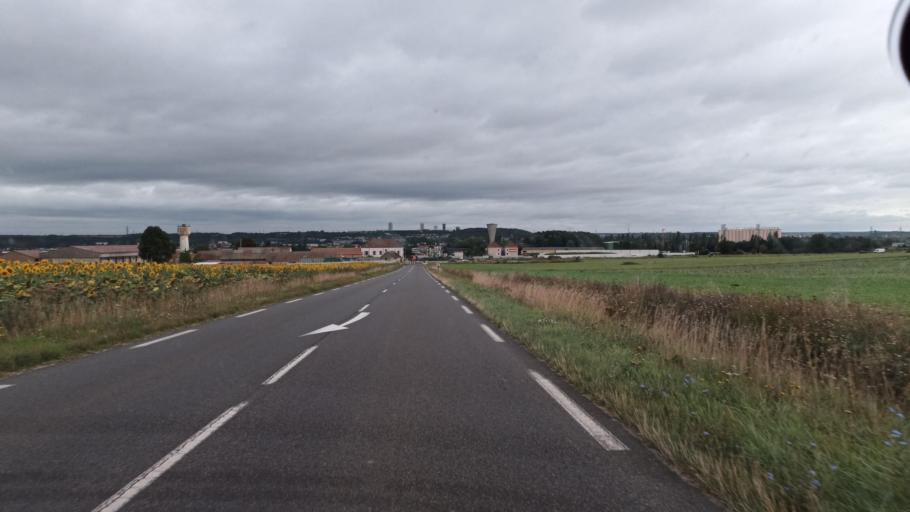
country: FR
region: Ile-de-France
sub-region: Departement de Seine-et-Marne
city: Montereau-Fault-Yonne
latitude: 48.3575
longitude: 2.9571
